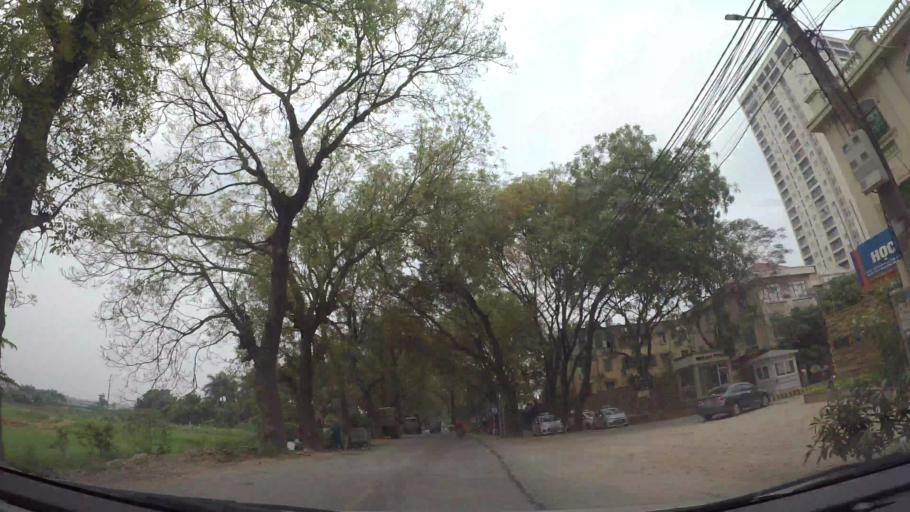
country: VN
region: Ha Noi
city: Cau Dien
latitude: 21.0160
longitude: 105.7453
